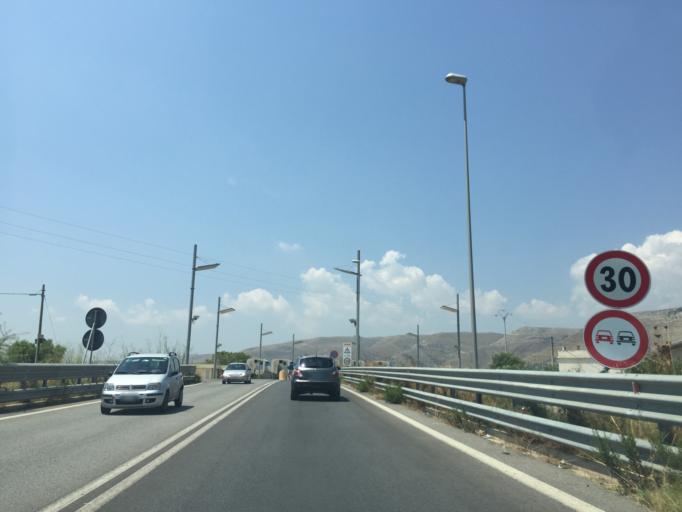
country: IT
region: Sicily
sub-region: Provincia di Siracusa
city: Avola
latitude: 36.9313
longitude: 15.1629
